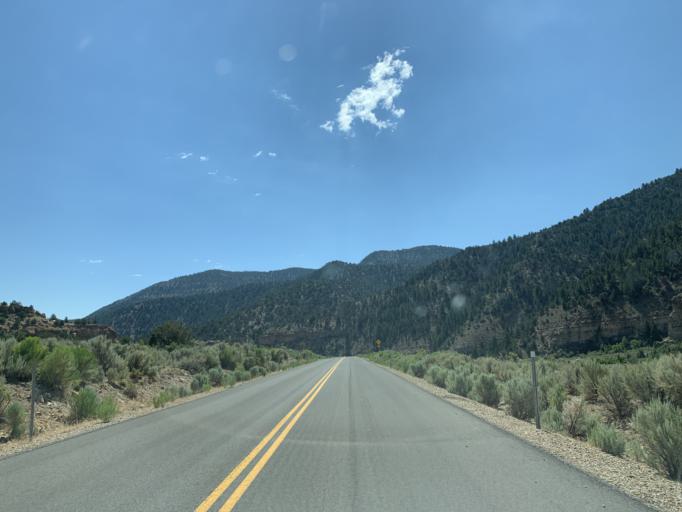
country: US
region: Utah
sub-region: Carbon County
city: East Carbon City
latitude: 39.7781
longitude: -110.4381
